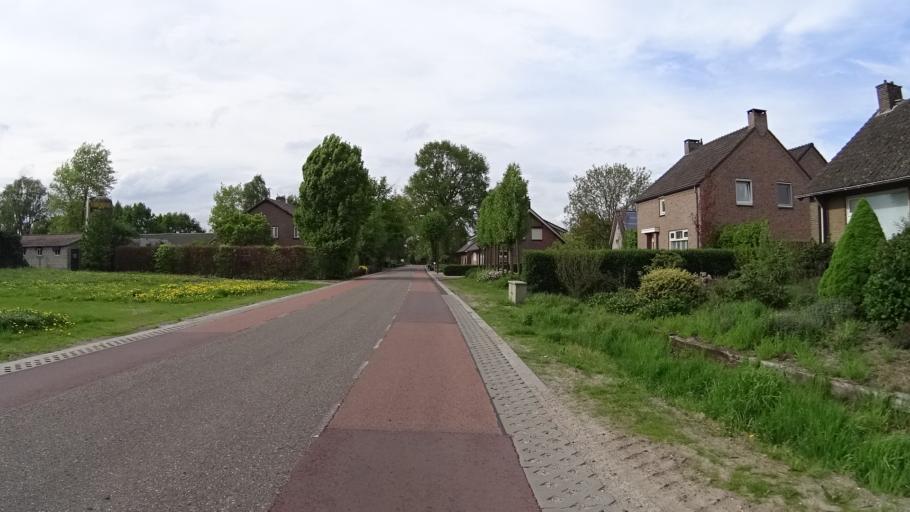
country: NL
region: North Brabant
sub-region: Gemeente Boekel
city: Boekel
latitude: 51.6140
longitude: 5.6804
